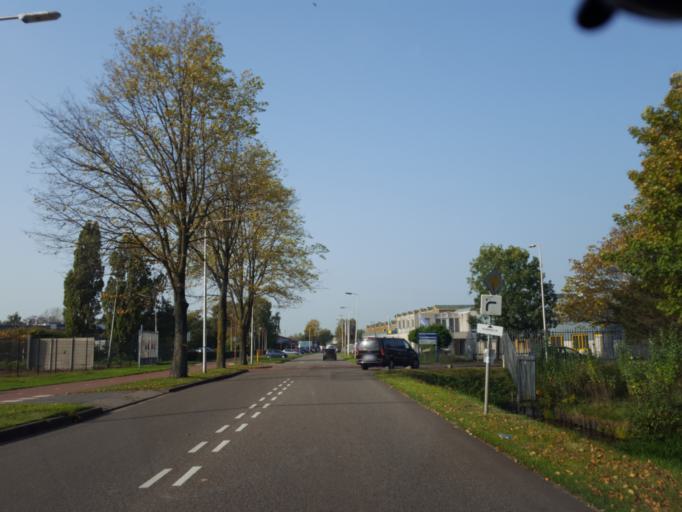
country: NL
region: Utrecht
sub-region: Gemeente Utrecht
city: Utrecht
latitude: 52.1019
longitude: 5.0829
